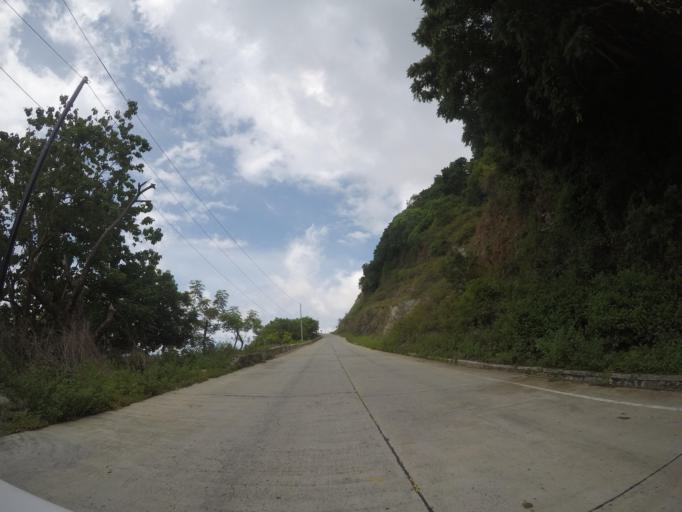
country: TL
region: Liquica
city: Maubara
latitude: -8.6671
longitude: 125.1100
